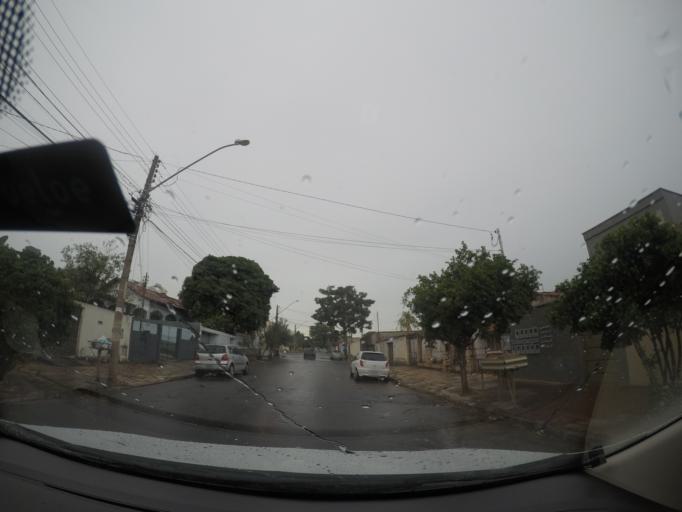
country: BR
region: Goias
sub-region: Goiania
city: Goiania
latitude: -16.6796
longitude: -49.2483
